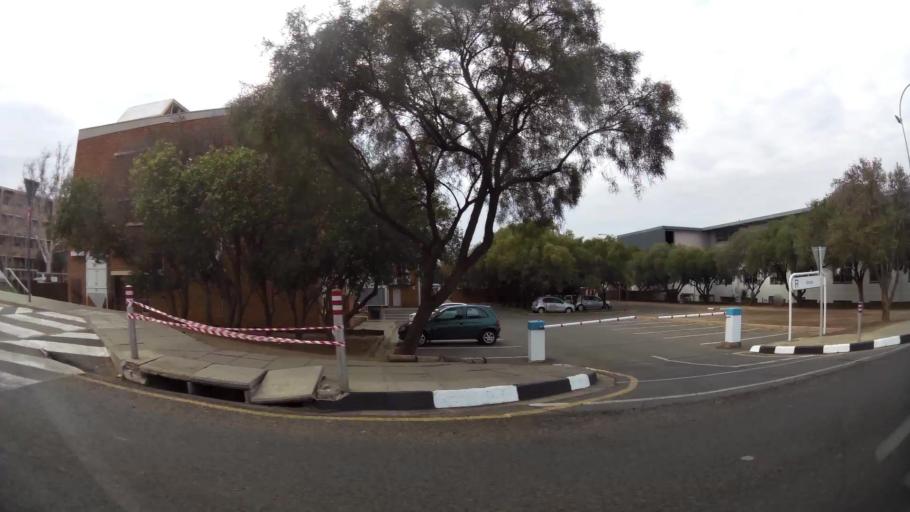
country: ZA
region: Orange Free State
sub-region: Mangaung Metropolitan Municipality
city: Bloemfontein
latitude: -29.1112
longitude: 26.1843
